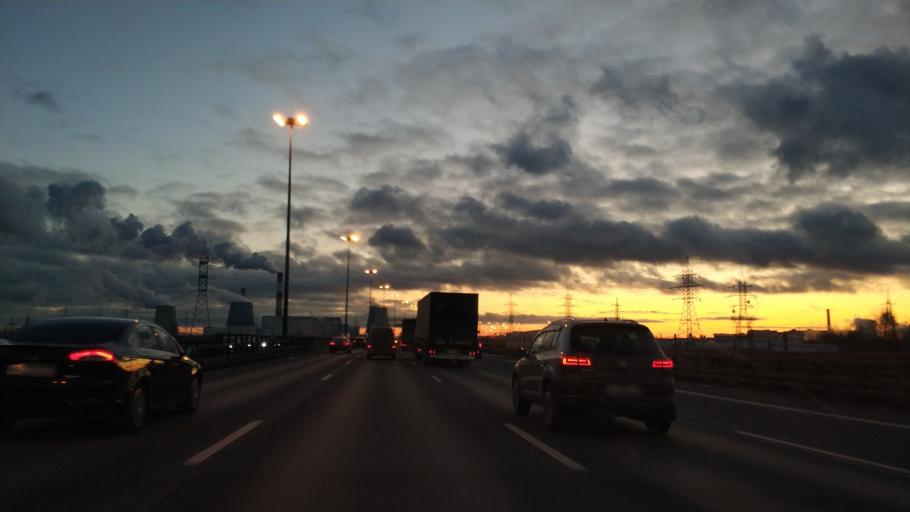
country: RU
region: St.-Petersburg
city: Obukhovo
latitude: 59.8435
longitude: 30.4566
